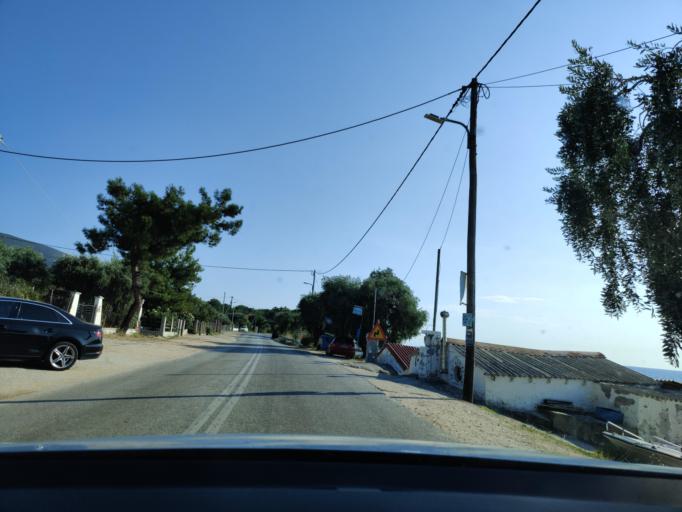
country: GR
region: East Macedonia and Thrace
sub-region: Nomos Kavalas
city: Prinos
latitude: 40.6997
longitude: 24.5278
